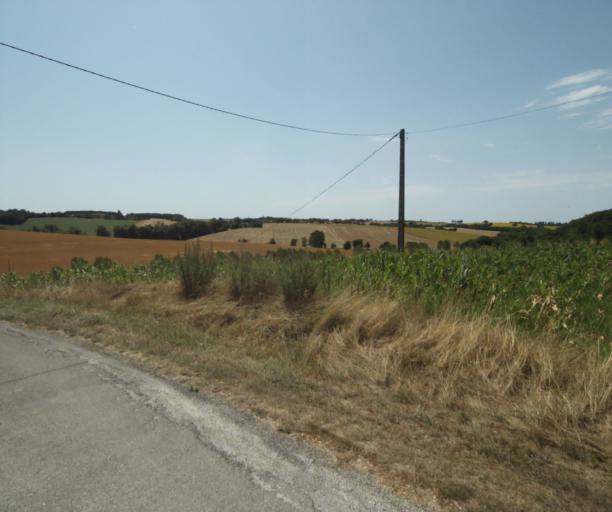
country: FR
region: Midi-Pyrenees
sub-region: Departement de la Haute-Garonne
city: Saint-Felix-Lauragais
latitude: 43.4644
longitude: 1.8620
